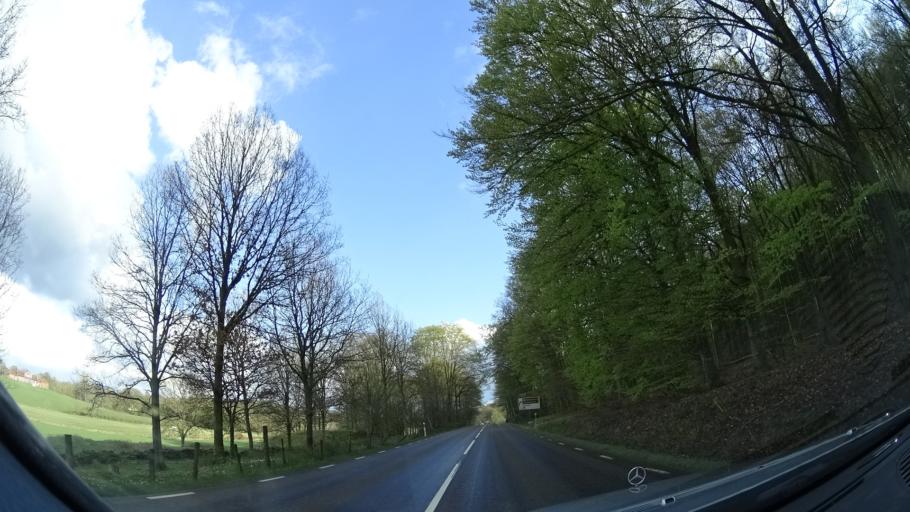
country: SE
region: Skane
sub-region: Klippans Kommun
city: Ljungbyhed
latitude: 56.0435
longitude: 13.2505
